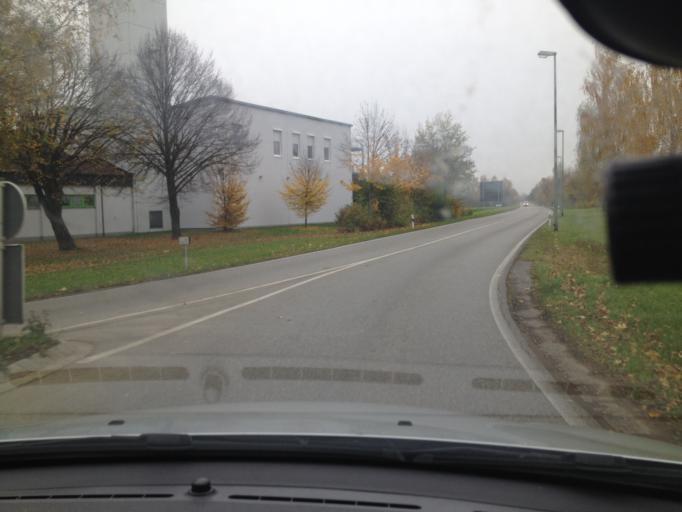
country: DE
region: Bavaria
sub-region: Swabia
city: Schwabmunchen
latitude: 48.1876
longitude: 10.7443
